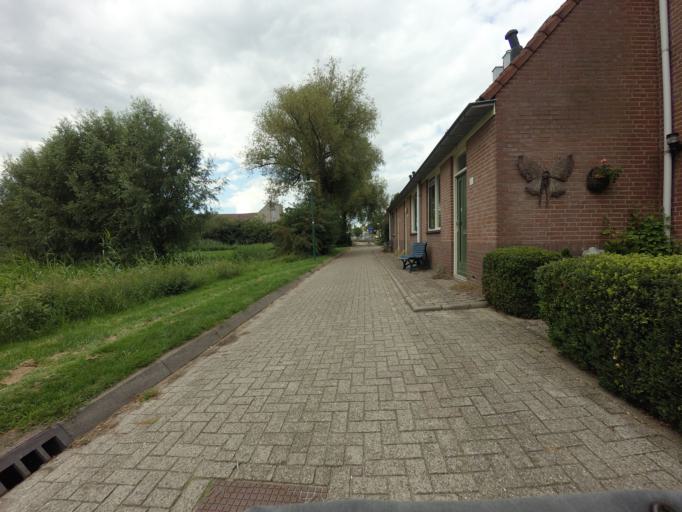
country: NL
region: Utrecht
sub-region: Gemeente IJsselstein
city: IJsselstein
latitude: 52.0212
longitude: 5.0297
